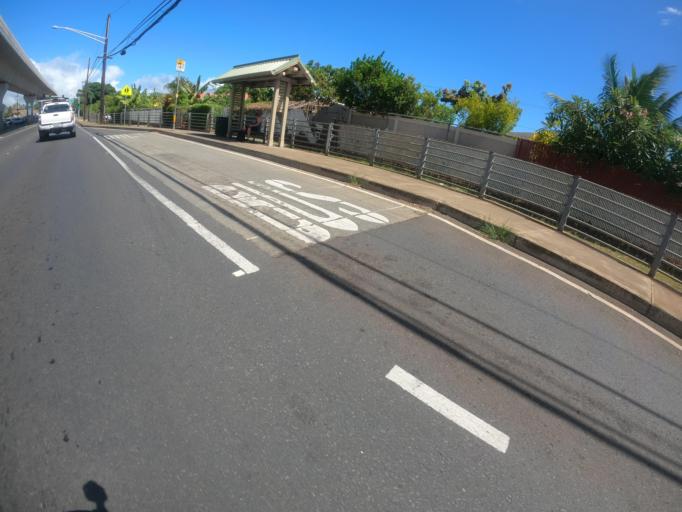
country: US
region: Hawaii
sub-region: Honolulu County
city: Waipahu
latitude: 21.3862
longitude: -157.9984
